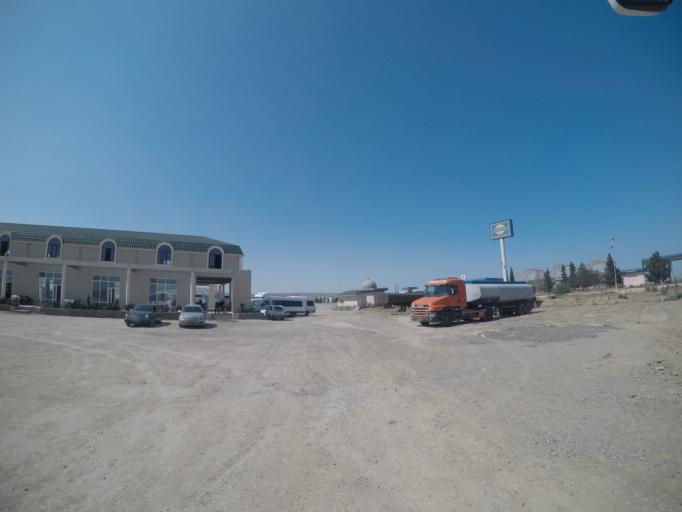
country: AZ
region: Baki
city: Qobustan
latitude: 39.9653
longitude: 49.4076
